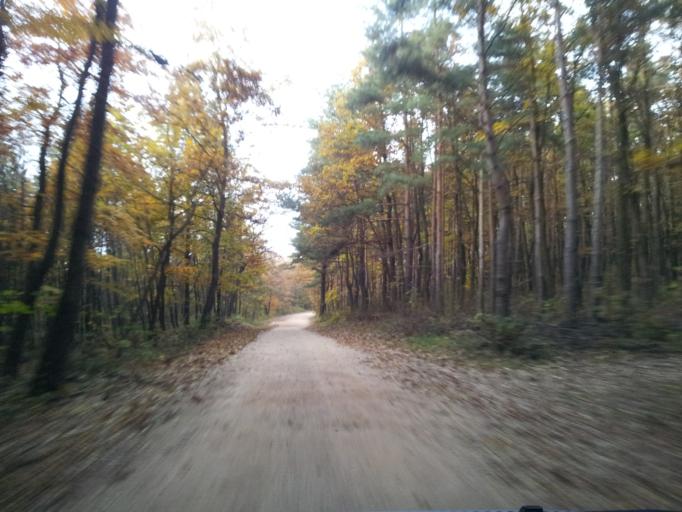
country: HU
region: Gyor-Moson-Sopron
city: Bakonyszentlaszlo
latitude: 47.3758
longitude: 17.8224
